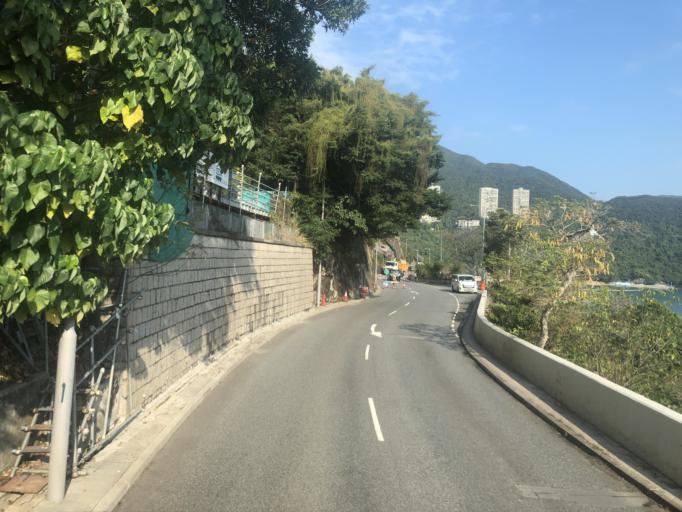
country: HK
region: Wanchai
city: Wan Chai
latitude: 22.2453
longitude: 114.1800
